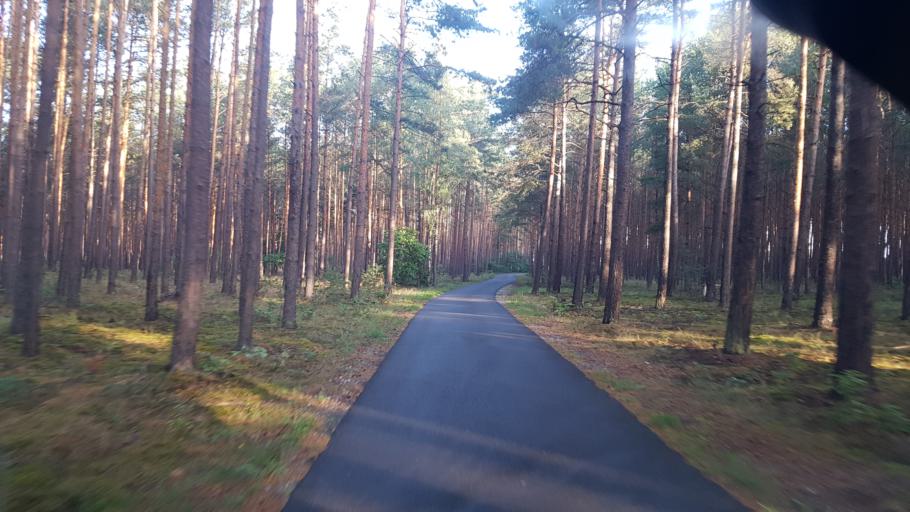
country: DE
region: Brandenburg
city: Bronkow
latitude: 51.6695
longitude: 13.8935
